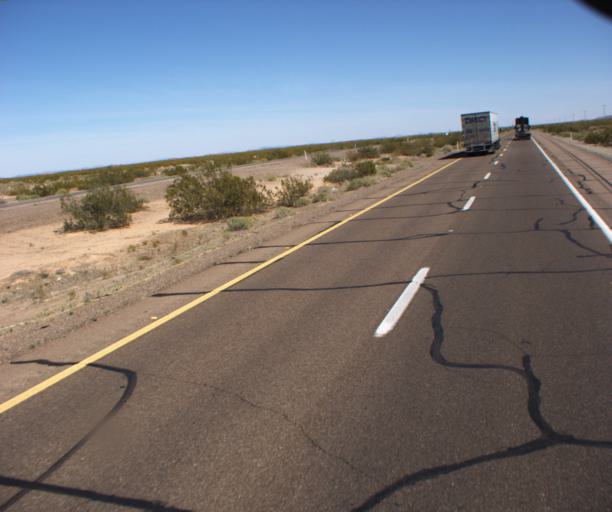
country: US
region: Arizona
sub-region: Yuma County
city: Wellton
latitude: 32.7697
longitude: -113.6115
